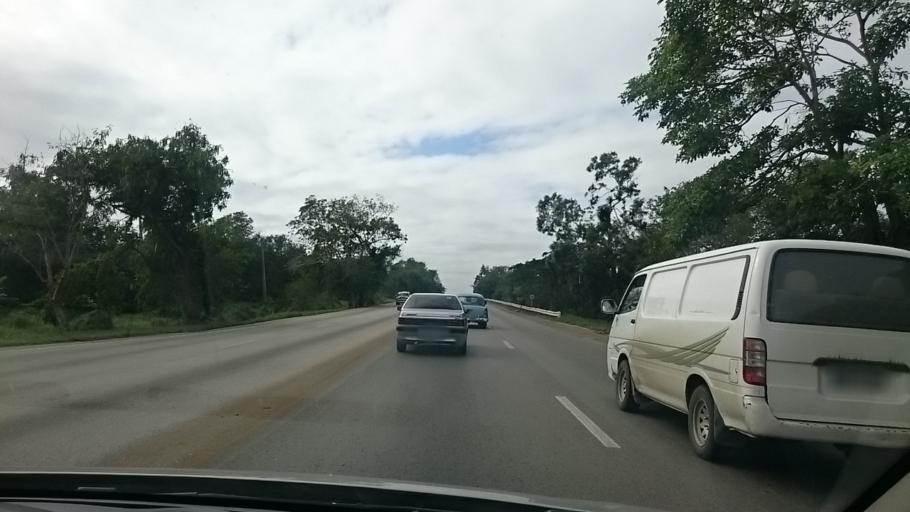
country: CU
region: La Habana
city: Alamar
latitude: 23.1553
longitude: -82.2714
